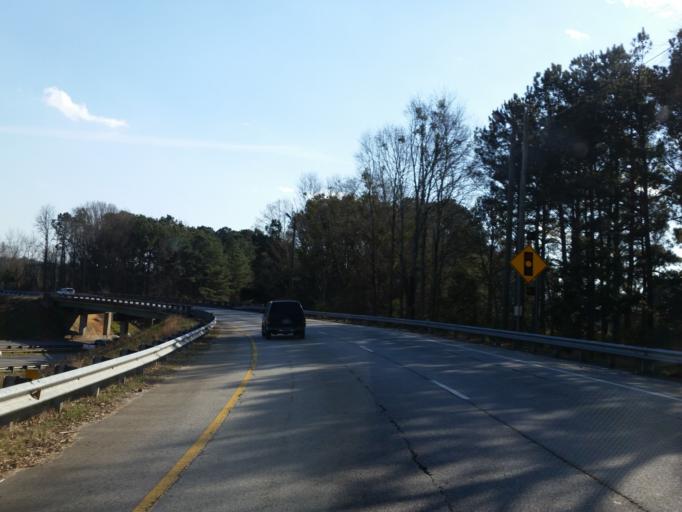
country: US
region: Georgia
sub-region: Spalding County
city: Experiment
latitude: 33.2637
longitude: -84.2906
